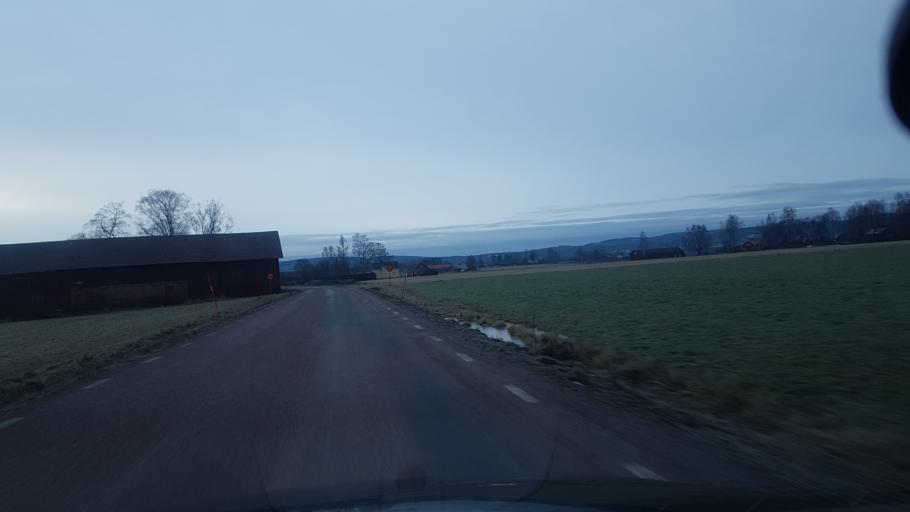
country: SE
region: Dalarna
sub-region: Saters Kommun
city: Saeter
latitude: 60.4313
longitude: 15.6559
